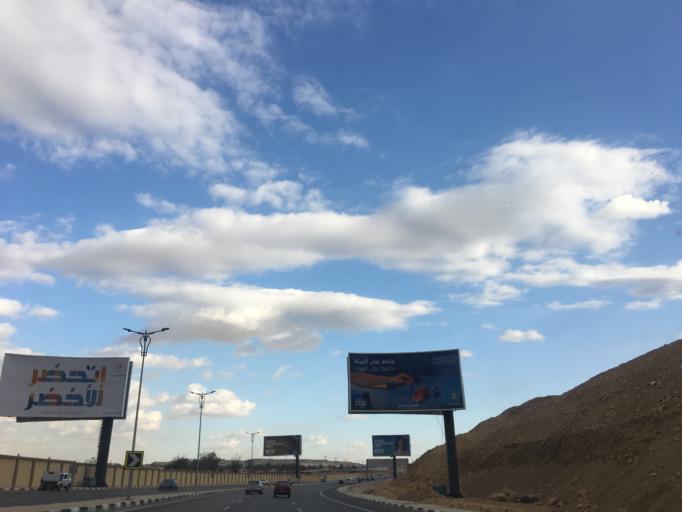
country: EG
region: Muhafazat al Qahirah
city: Cairo
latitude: 30.0262
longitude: 31.3205
